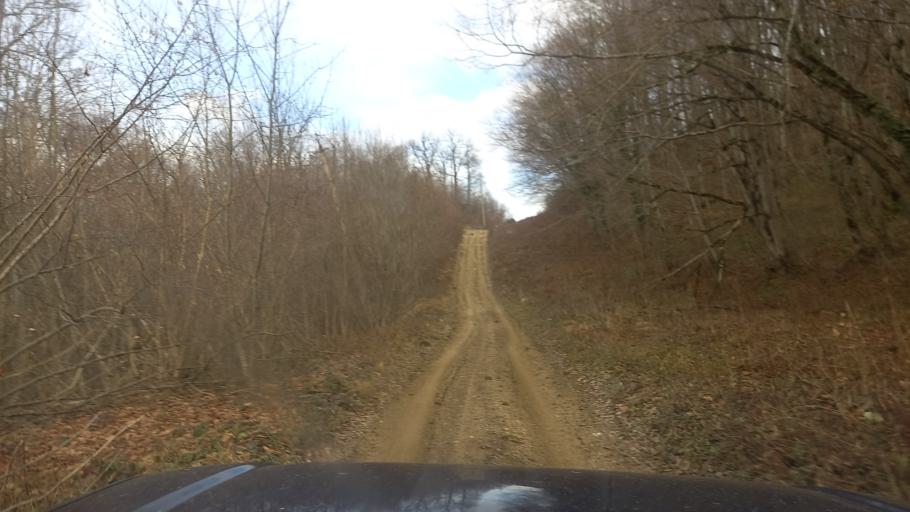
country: RU
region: Krasnodarskiy
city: Neftegorsk
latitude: 44.2046
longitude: 39.7056
